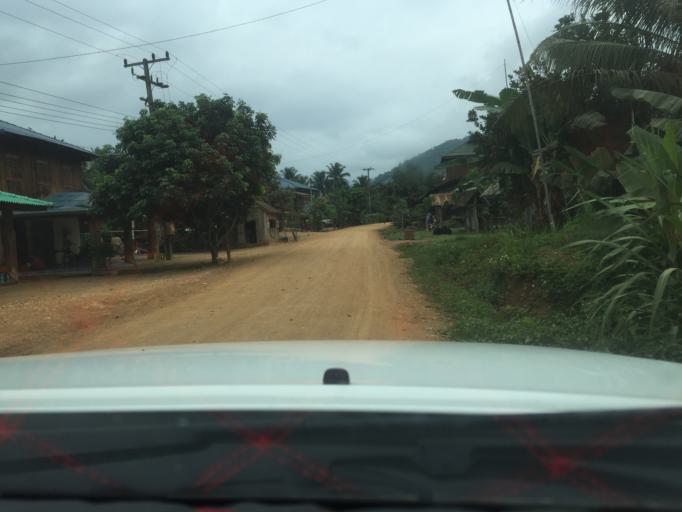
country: TH
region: Phayao
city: Phu Sang
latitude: 19.6882
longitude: 100.5020
